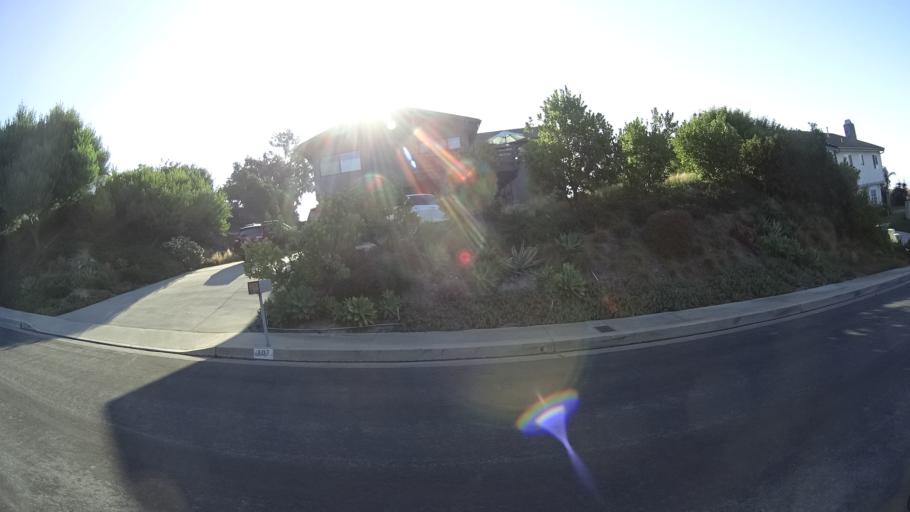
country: US
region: California
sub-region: Orange County
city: San Clemente
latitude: 33.4163
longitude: -117.5893
